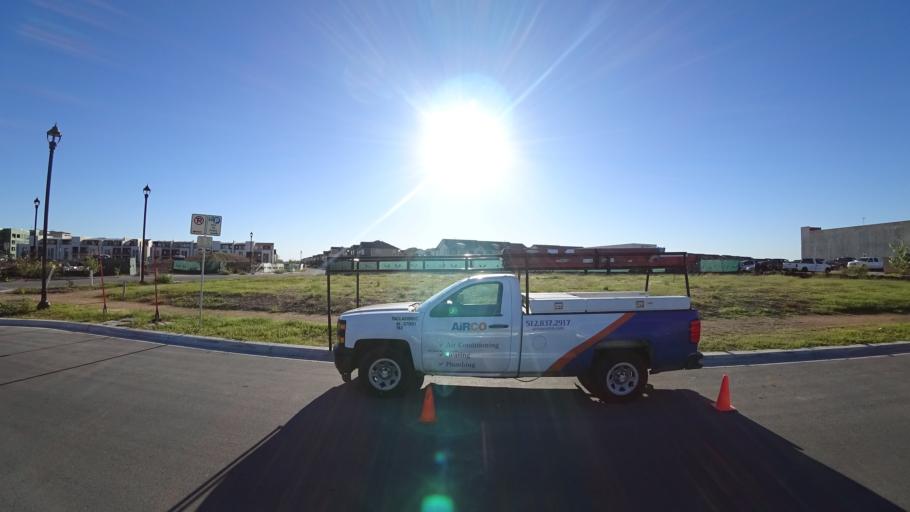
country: US
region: Texas
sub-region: Travis County
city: Austin
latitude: 30.3000
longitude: -97.7039
